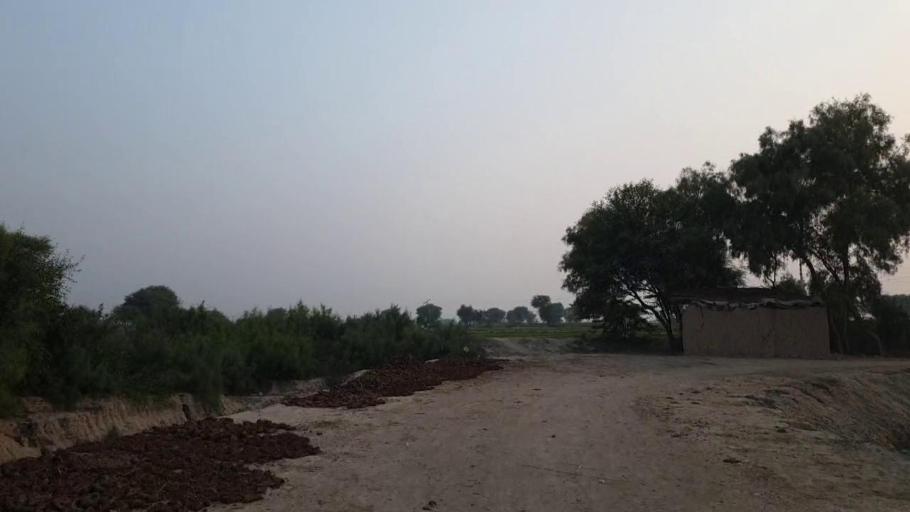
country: PK
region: Sindh
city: Bhan
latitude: 26.5304
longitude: 67.7066
